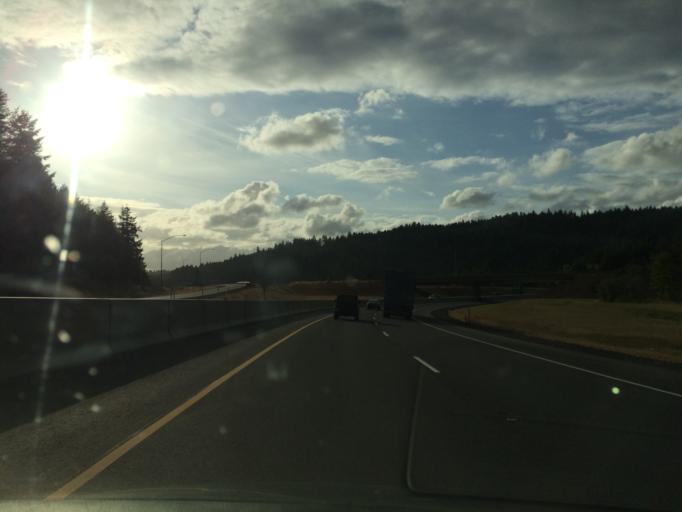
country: US
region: Oregon
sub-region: Douglas County
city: Drain
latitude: 43.7073
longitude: -123.2147
